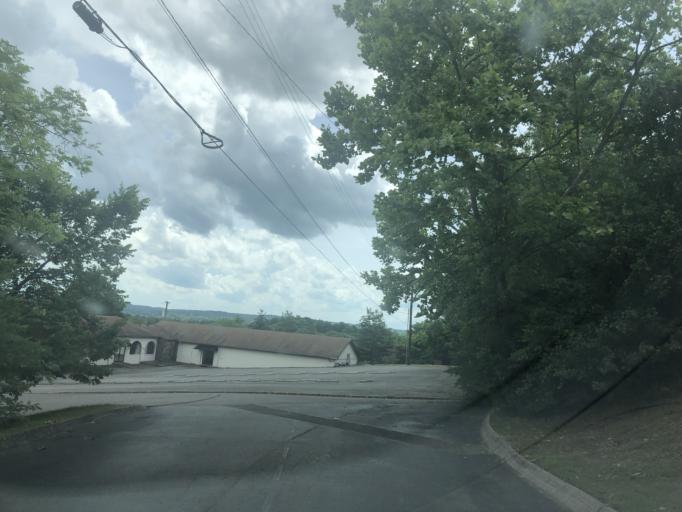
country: US
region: Tennessee
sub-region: Davidson County
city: Belle Meade
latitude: 36.0775
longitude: -86.9223
